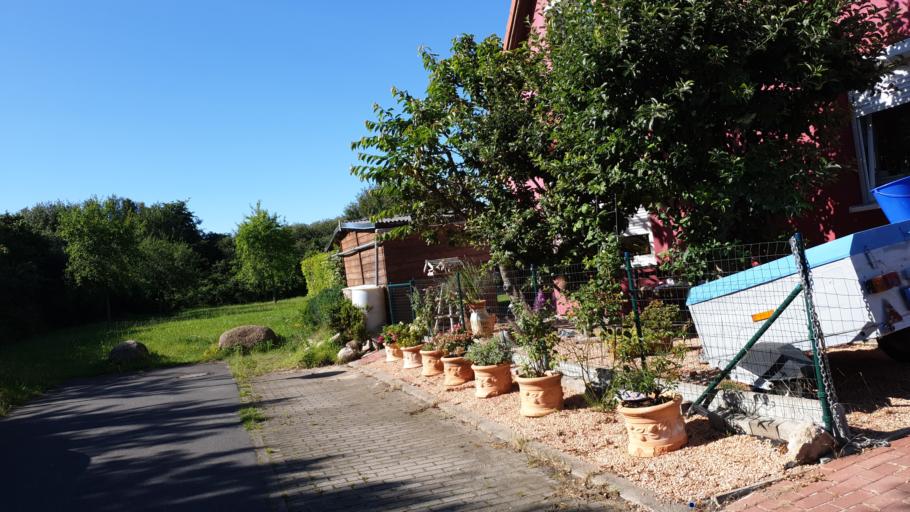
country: DE
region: Mecklenburg-Vorpommern
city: Kramerhof
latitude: 54.3420
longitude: 13.0623
